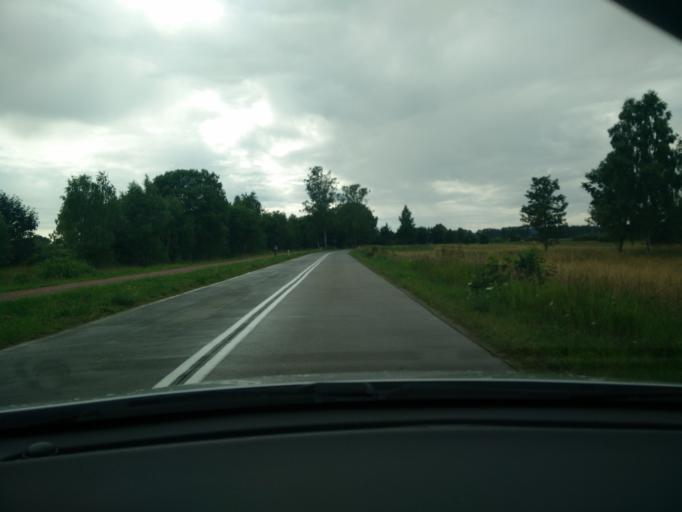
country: PL
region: Pomeranian Voivodeship
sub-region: Powiat pucki
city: Mrzezino
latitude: 54.6221
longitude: 18.4428
